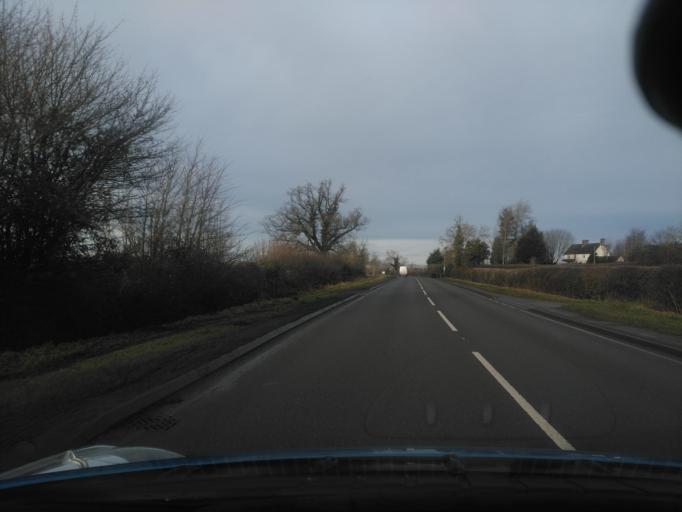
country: GB
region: England
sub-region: Gloucestershire
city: Moreton in Marsh
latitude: 51.9725
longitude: -1.6333
